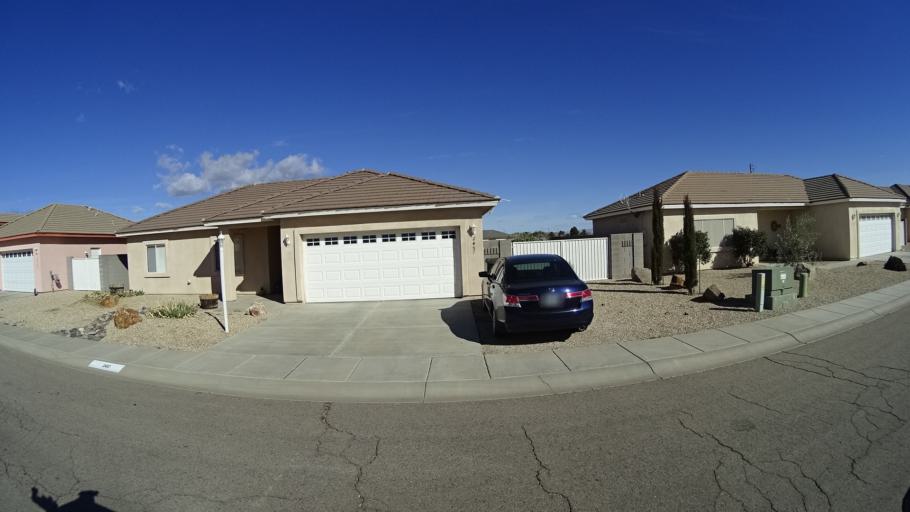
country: US
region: Arizona
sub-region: Mohave County
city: New Kingman-Butler
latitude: 35.2354
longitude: -114.0218
